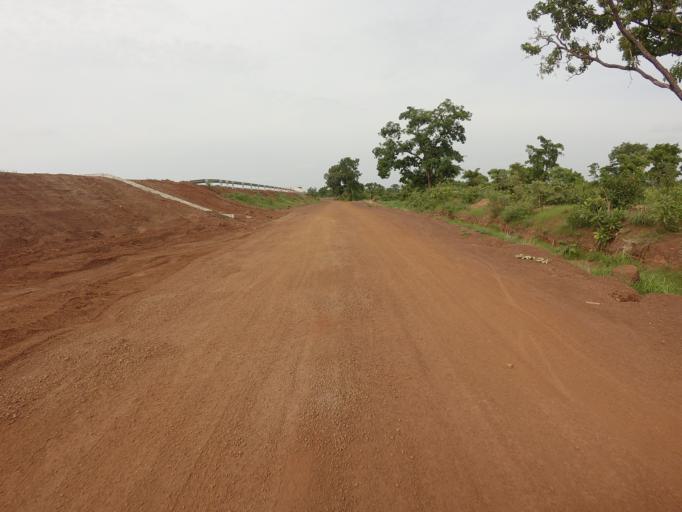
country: GH
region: Northern
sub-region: Yendi
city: Yendi
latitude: 9.7934
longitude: -0.1147
